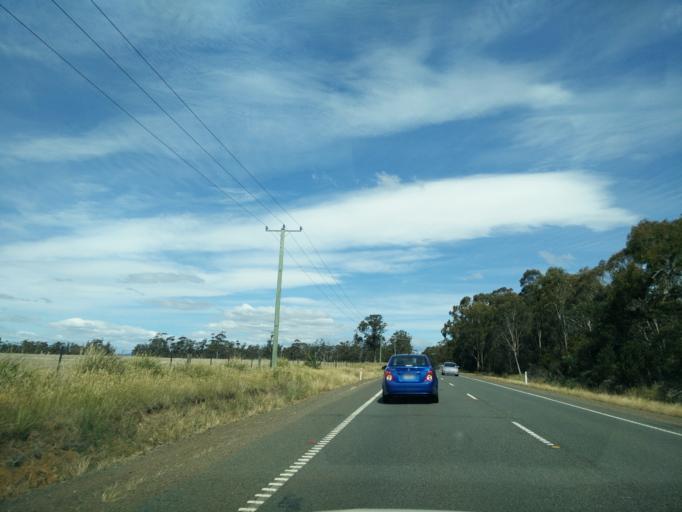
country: AU
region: Tasmania
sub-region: Northern Midlands
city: Evandale
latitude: -41.7835
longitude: 147.3777
